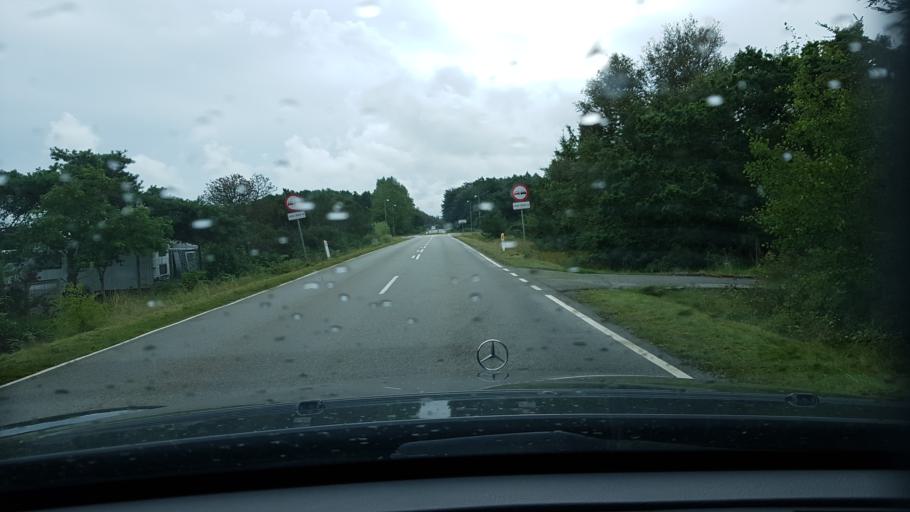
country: DK
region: North Denmark
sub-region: Alborg Kommune
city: Hals
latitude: 56.8218
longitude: 10.2694
